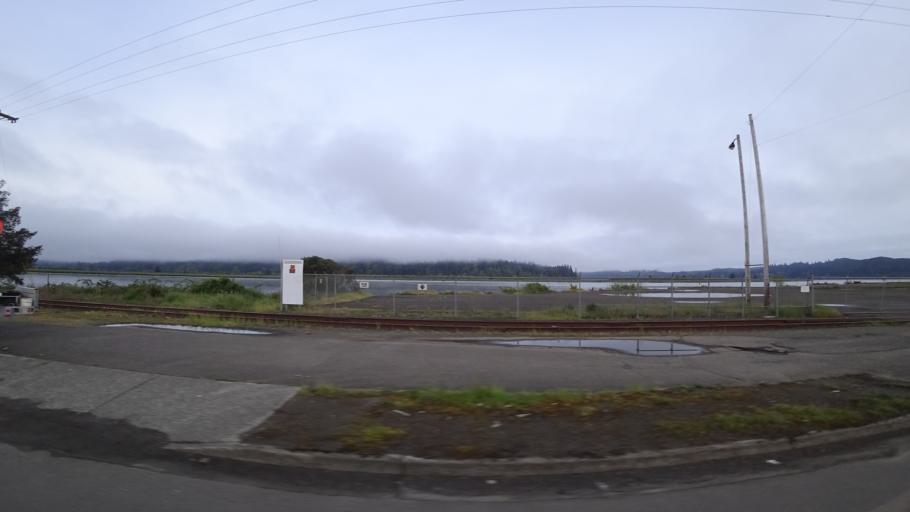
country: US
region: Oregon
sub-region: Douglas County
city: Reedsport
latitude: 43.7301
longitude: -124.1118
